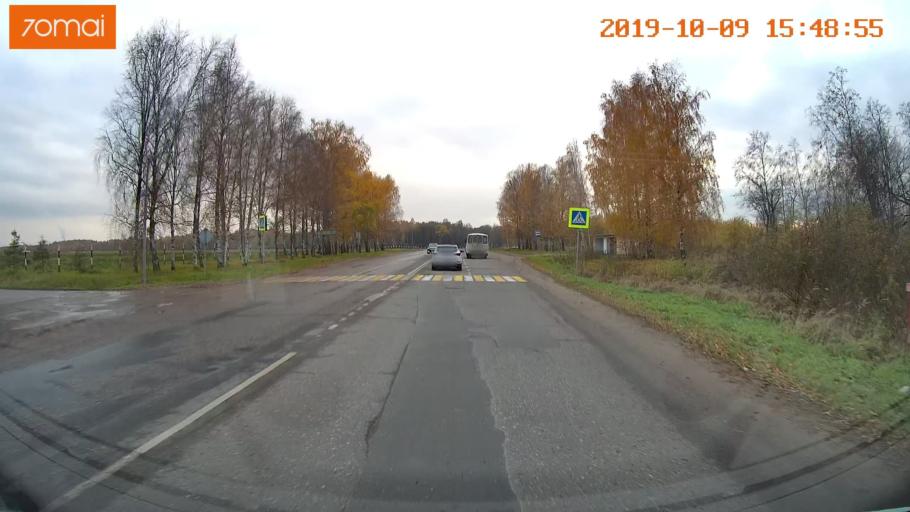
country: RU
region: Kostroma
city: Oktyabr'skiy
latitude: 57.8088
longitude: 41.0106
